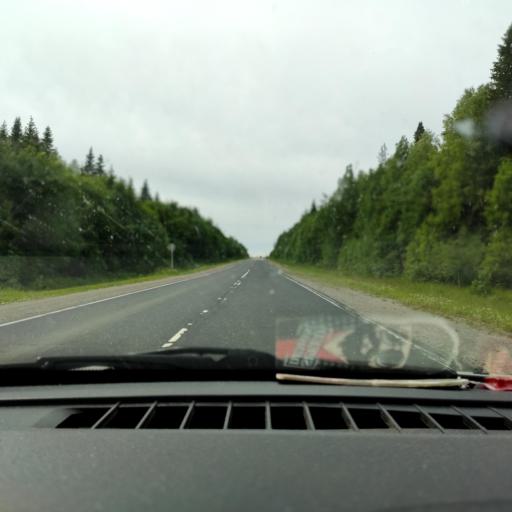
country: RU
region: Perm
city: Chusovoy
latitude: 58.3739
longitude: 57.9759
